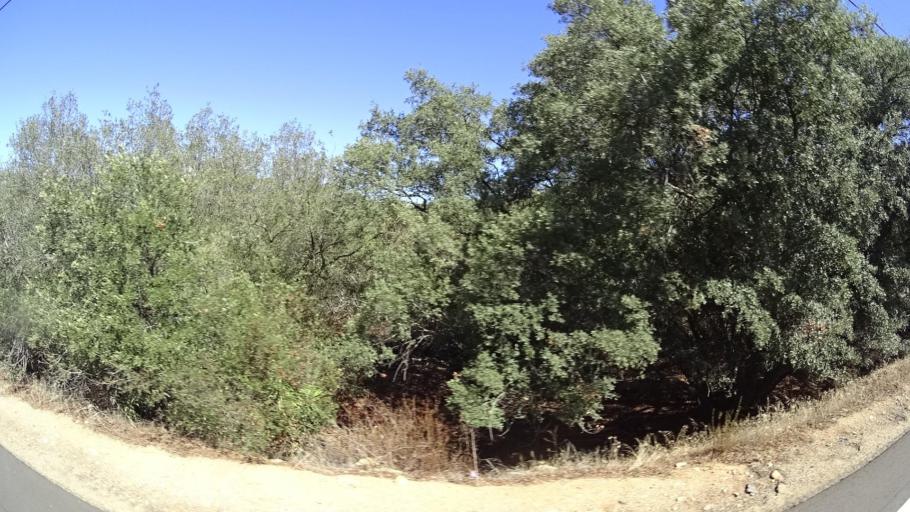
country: US
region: California
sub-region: San Diego County
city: Jamul
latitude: 32.7262
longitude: -116.7718
